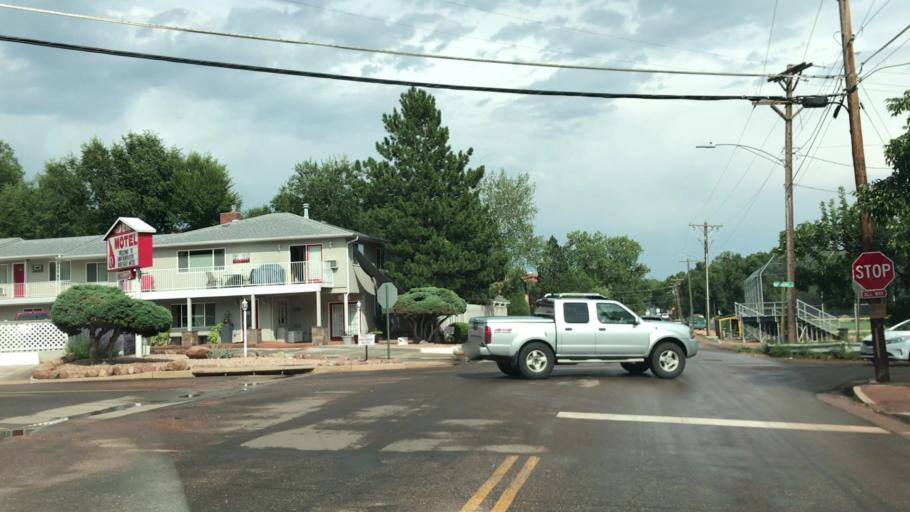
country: US
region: Colorado
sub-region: El Paso County
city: Manitou Springs
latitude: 38.8595
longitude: -104.8917
